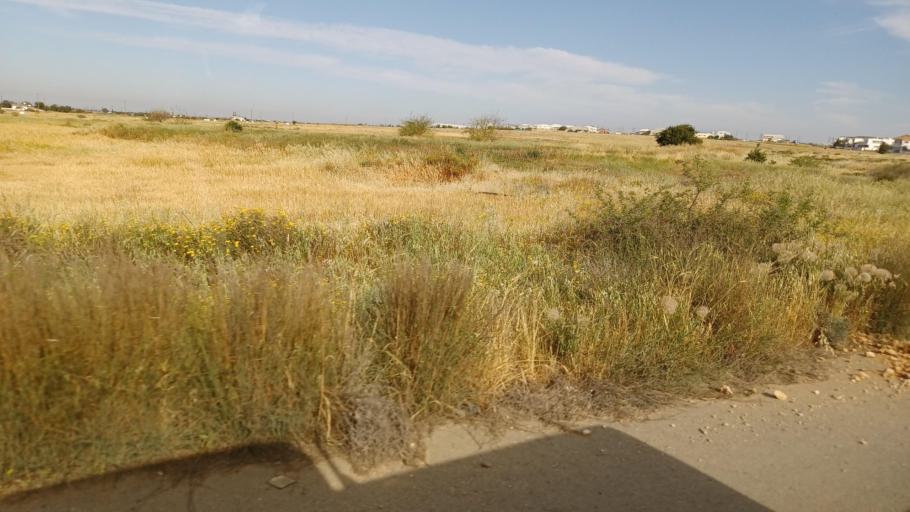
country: CY
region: Lefkosia
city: Kokkinotrimithia
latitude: 35.1635
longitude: 33.1994
